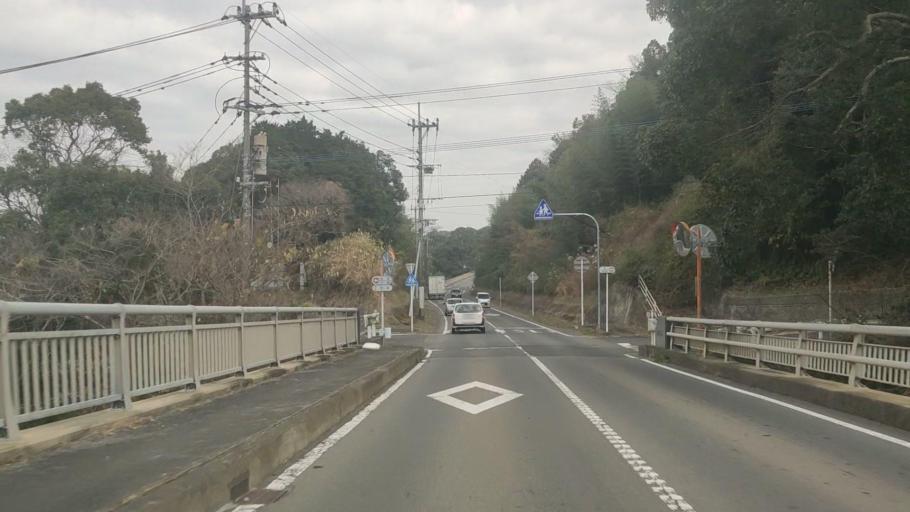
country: JP
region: Nagasaki
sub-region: Isahaya-shi
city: Isahaya
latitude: 32.8126
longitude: 130.1722
